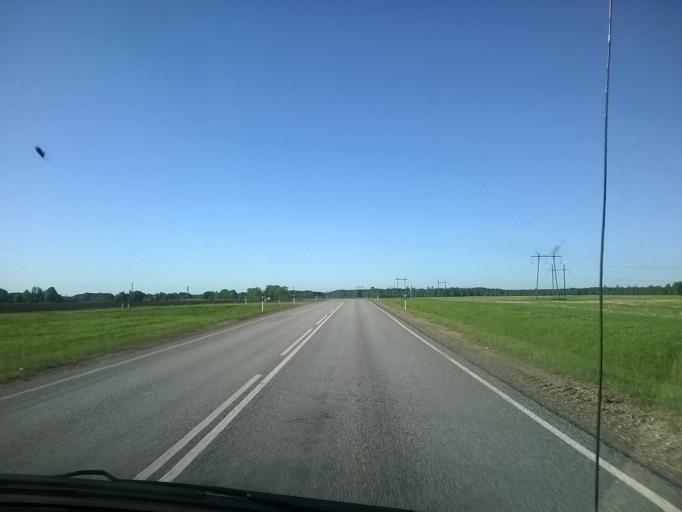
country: EE
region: Valgamaa
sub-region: Valga linn
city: Valga
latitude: 57.9433
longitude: 26.1685
